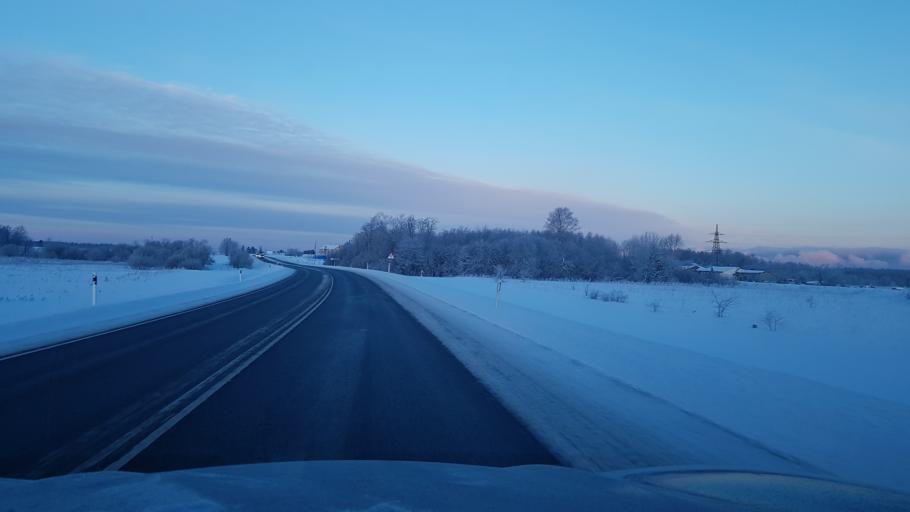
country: EE
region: Ida-Virumaa
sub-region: Narva-Joesuu linn
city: Narva-Joesuu
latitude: 59.4001
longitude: 28.0695
